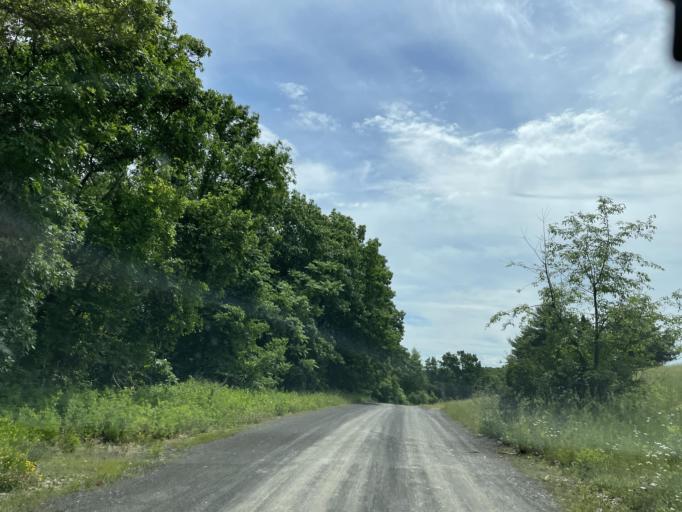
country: US
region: New York
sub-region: Ulster County
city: Lincoln Park
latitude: 41.9646
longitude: -74.0251
